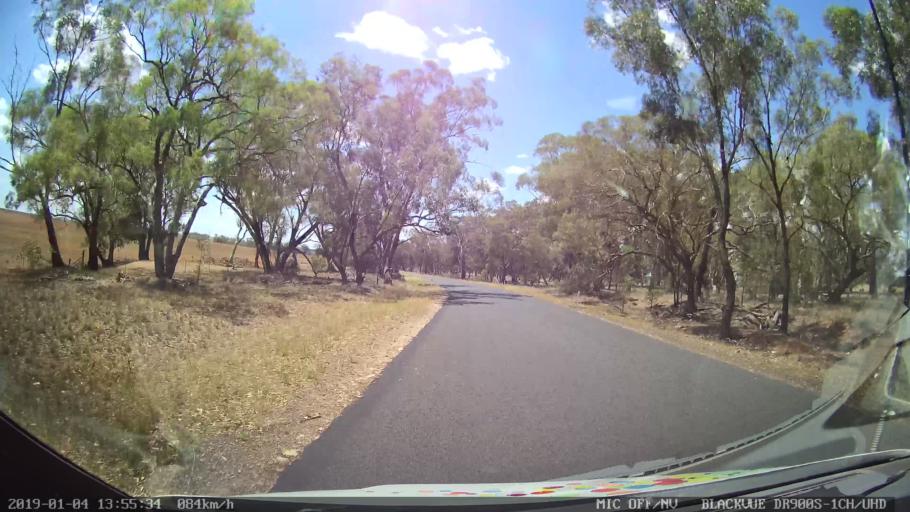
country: AU
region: New South Wales
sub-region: Dubbo Municipality
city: Dubbo
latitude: -32.3608
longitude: 148.5886
